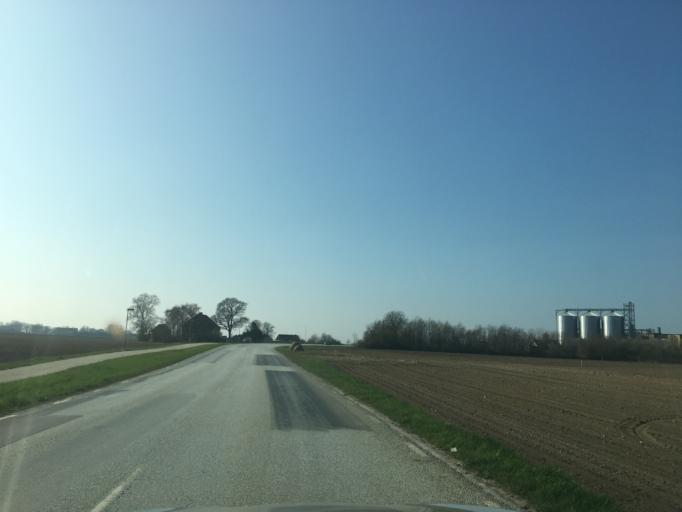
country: SE
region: Skane
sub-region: Staffanstorps Kommun
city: Staffanstorp
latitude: 55.6668
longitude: 13.1910
